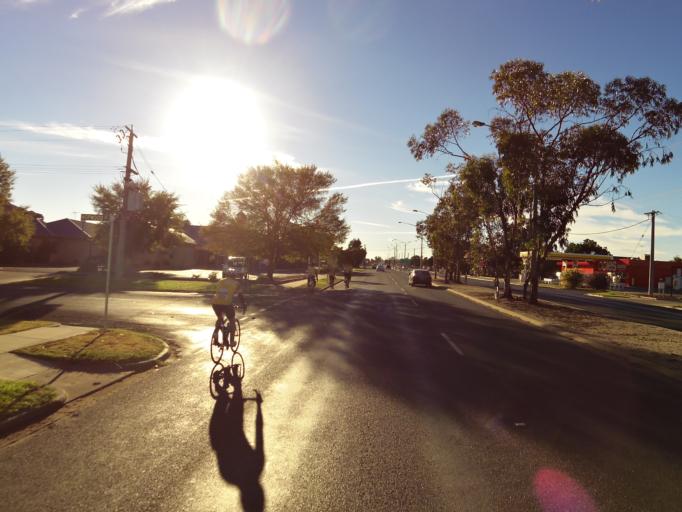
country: AU
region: Victoria
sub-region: Campaspe
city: Echuca
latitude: -36.1404
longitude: 144.7478
